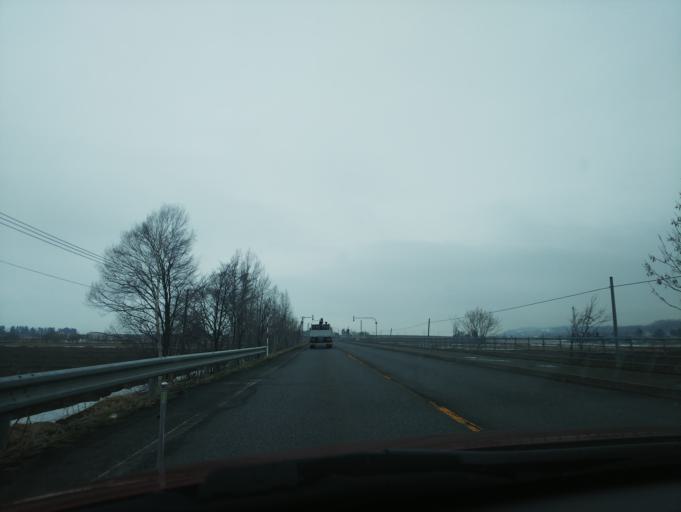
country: JP
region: Hokkaido
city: Nayoro
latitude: 44.0661
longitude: 142.3980
